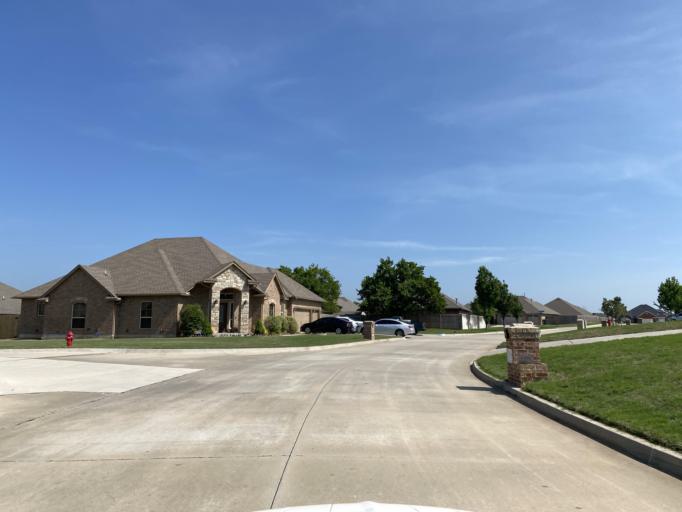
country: US
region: Oklahoma
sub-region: Oklahoma County
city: Nicoma Park
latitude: 35.4751
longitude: -97.3393
